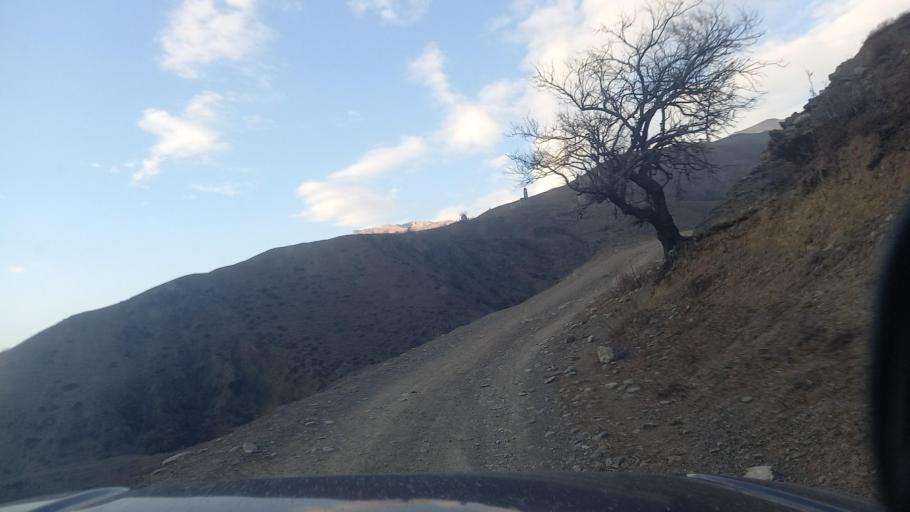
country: RU
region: Ingushetiya
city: Dzhayrakh
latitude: 42.8037
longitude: 44.7533
